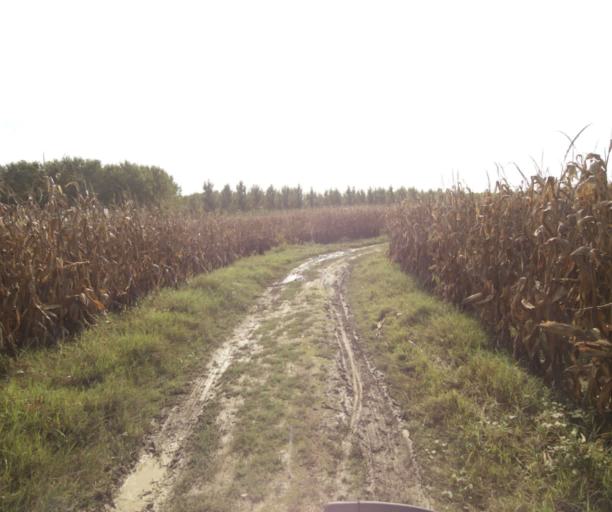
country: FR
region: Midi-Pyrenees
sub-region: Departement du Tarn-et-Garonne
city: Finhan
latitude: 43.9080
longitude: 1.2118
